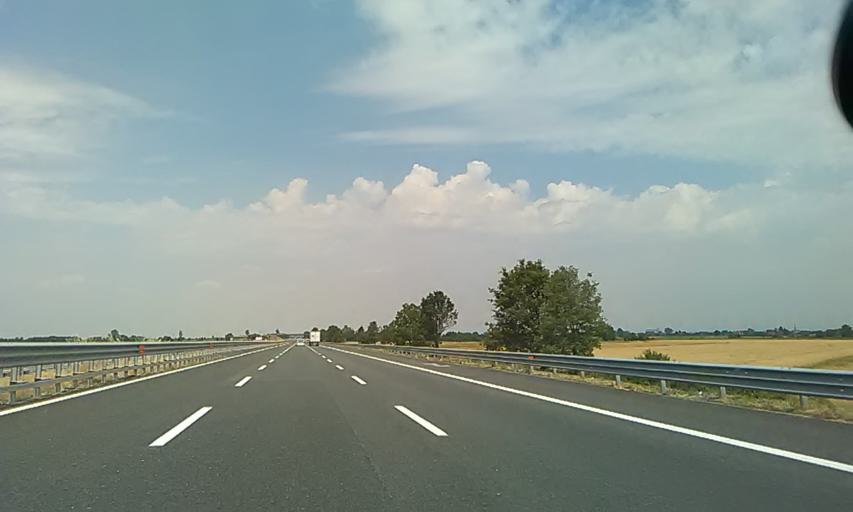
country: IT
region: Piedmont
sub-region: Provincia di Alessandria
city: Predosa
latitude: 44.7724
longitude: 8.6291
